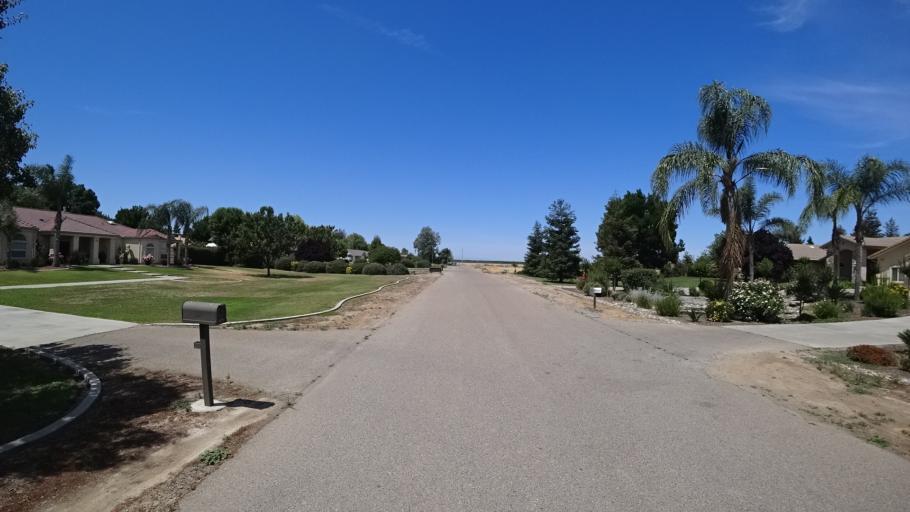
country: US
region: California
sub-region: Kings County
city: Armona
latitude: 36.3442
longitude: -119.7138
